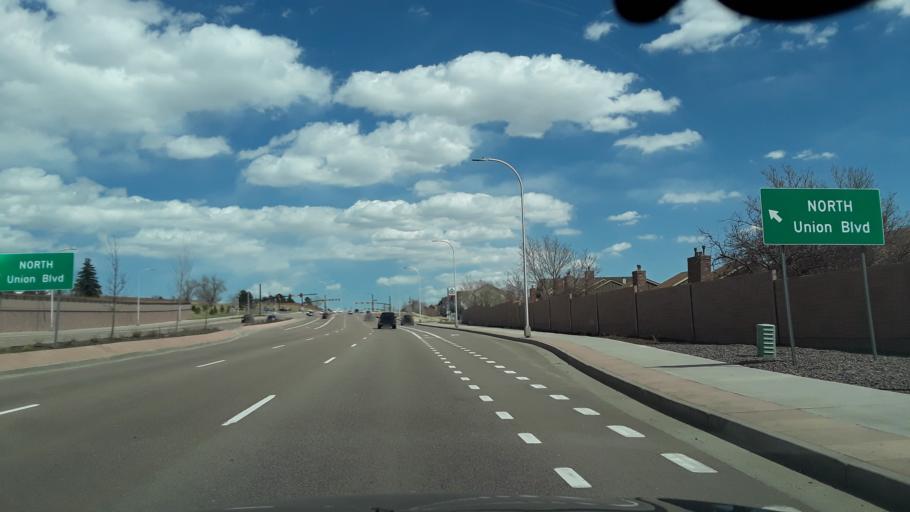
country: US
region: Colorado
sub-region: El Paso County
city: Air Force Academy
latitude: 38.9331
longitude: -104.7803
